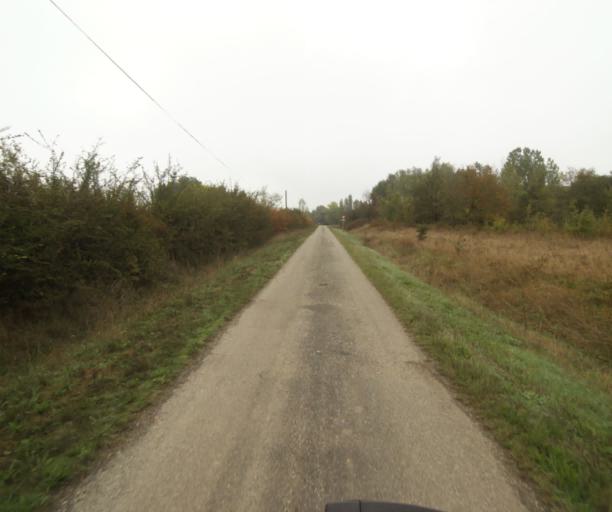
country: FR
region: Midi-Pyrenees
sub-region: Departement du Tarn-et-Garonne
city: Orgueil
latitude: 43.9062
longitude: 1.4176
